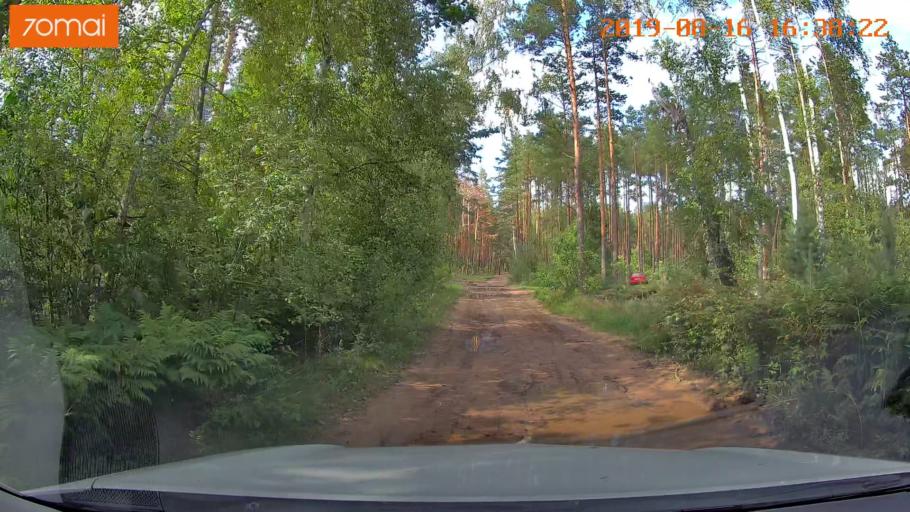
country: BY
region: Mogilev
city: Asipovichy
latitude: 53.2338
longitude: 28.7774
